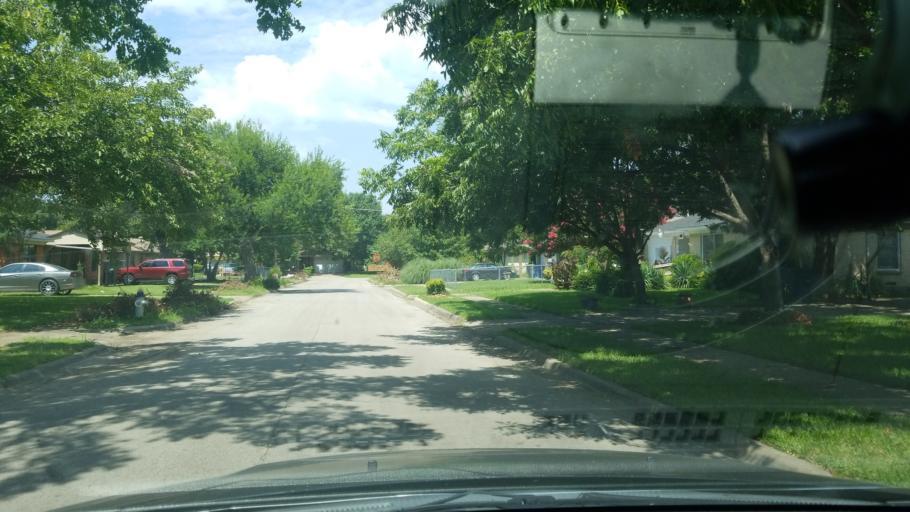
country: US
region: Texas
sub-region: Dallas County
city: Balch Springs
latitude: 32.7471
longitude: -96.6898
